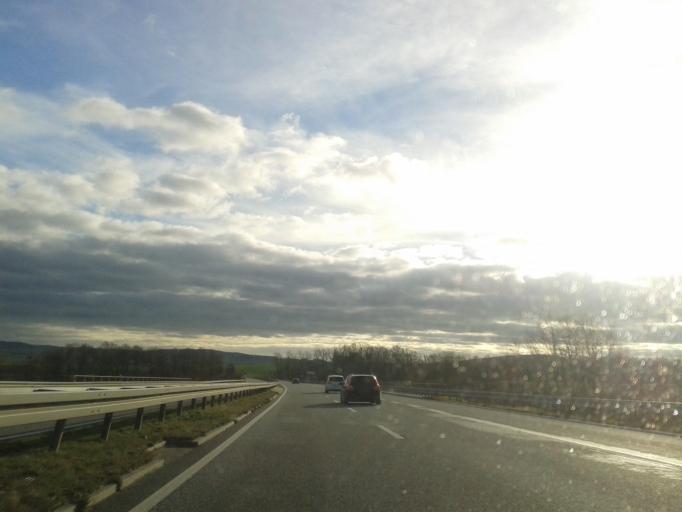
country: DE
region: Saxony
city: Grossschweidnitz
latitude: 51.0895
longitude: 14.6426
